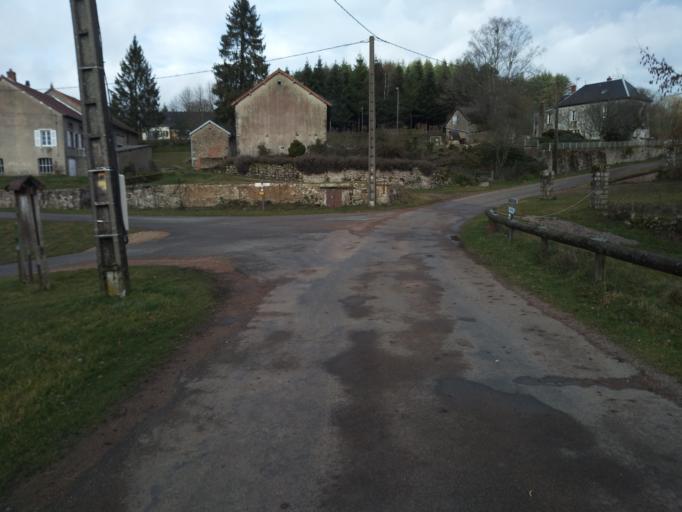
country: FR
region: Bourgogne
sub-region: Departement de la Cote-d'Or
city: Saulieu
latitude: 47.2757
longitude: 4.1439
